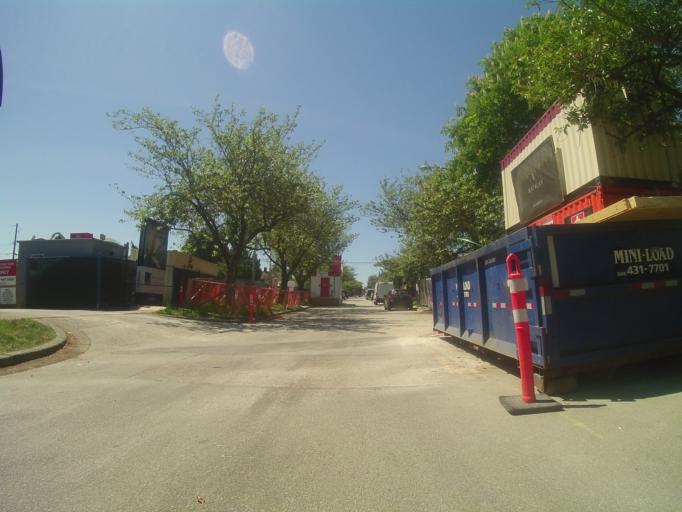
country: CA
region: British Columbia
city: Vancouver
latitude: 49.2132
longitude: -123.1152
